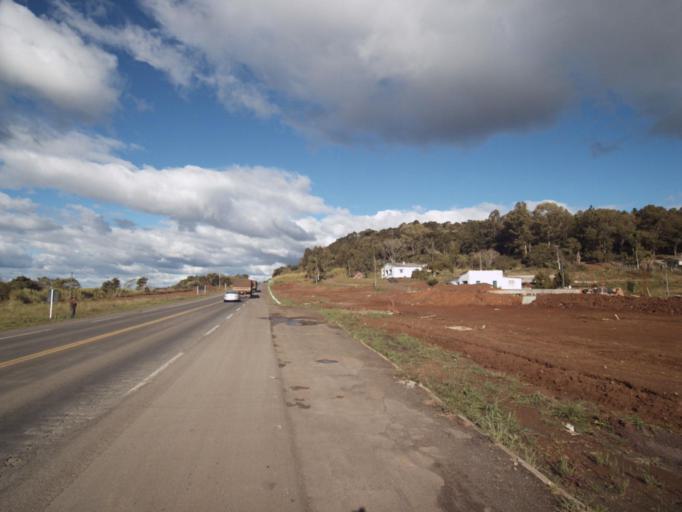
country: BR
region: Santa Catarina
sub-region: Joacaba
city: Joacaba
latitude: -27.1737
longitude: -51.5528
